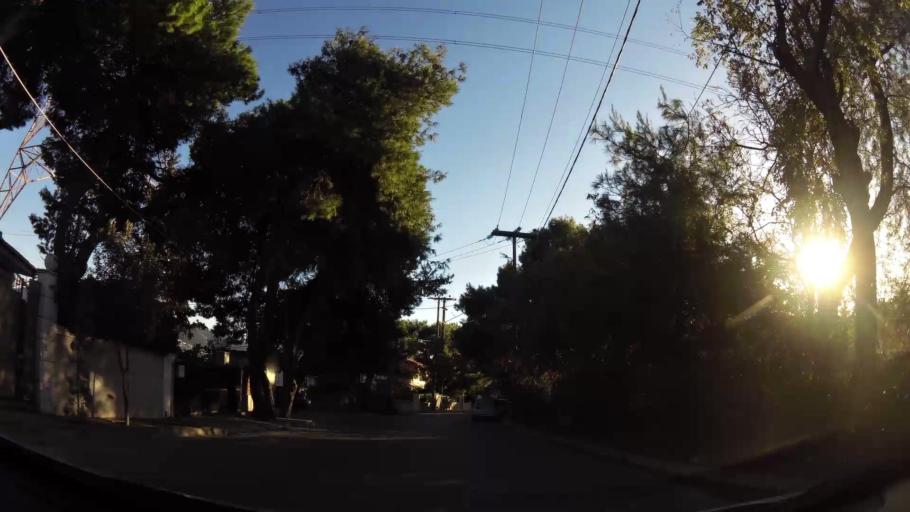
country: GR
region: Attica
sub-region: Nomarchia Anatolikis Attikis
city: Kryoneri
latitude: 38.1340
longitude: 23.8319
